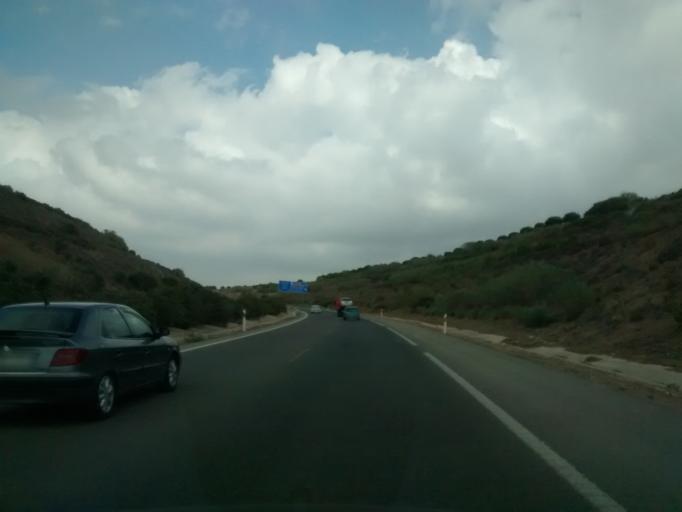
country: ES
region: Andalusia
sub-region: Provincia de Cadiz
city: Conil de la Frontera
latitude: 36.3419
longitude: -6.0503
